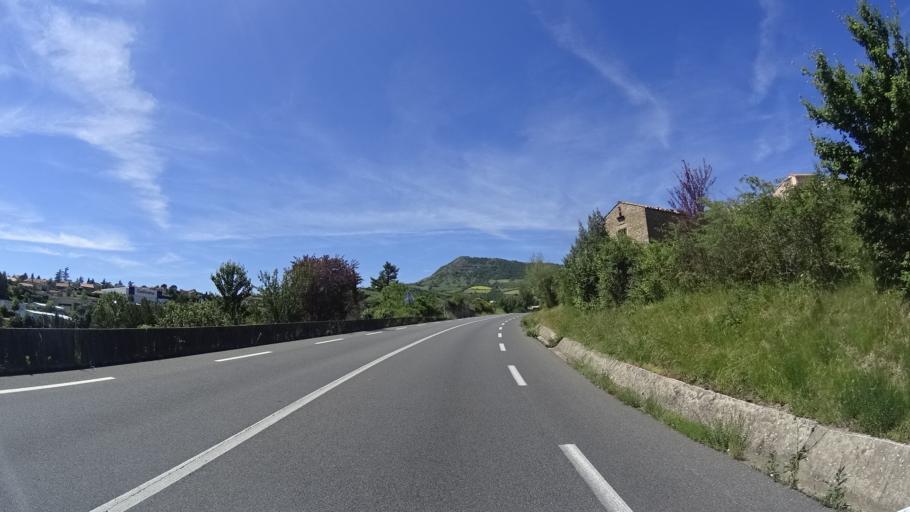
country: FR
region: Midi-Pyrenees
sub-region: Departement de l'Aveyron
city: Millau
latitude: 44.1143
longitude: 3.0754
